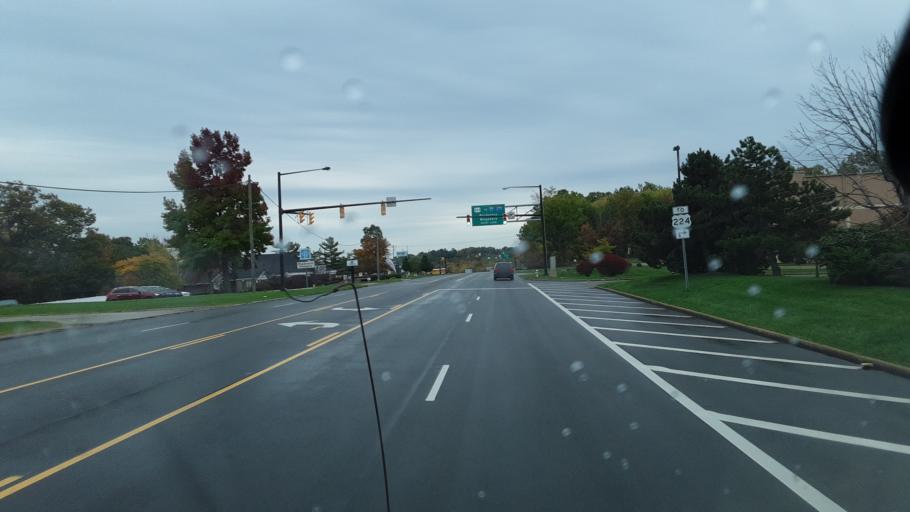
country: US
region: Ohio
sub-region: Summit County
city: Sawyerwood
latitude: 41.0285
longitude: -81.4858
